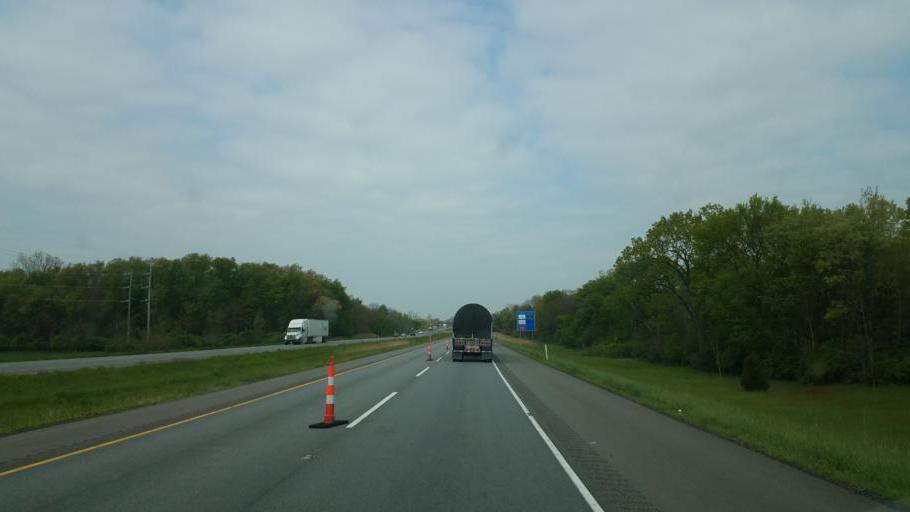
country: US
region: Indiana
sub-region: Saint Joseph County
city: Georgetown
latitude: 41.7165
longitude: -86.2265
